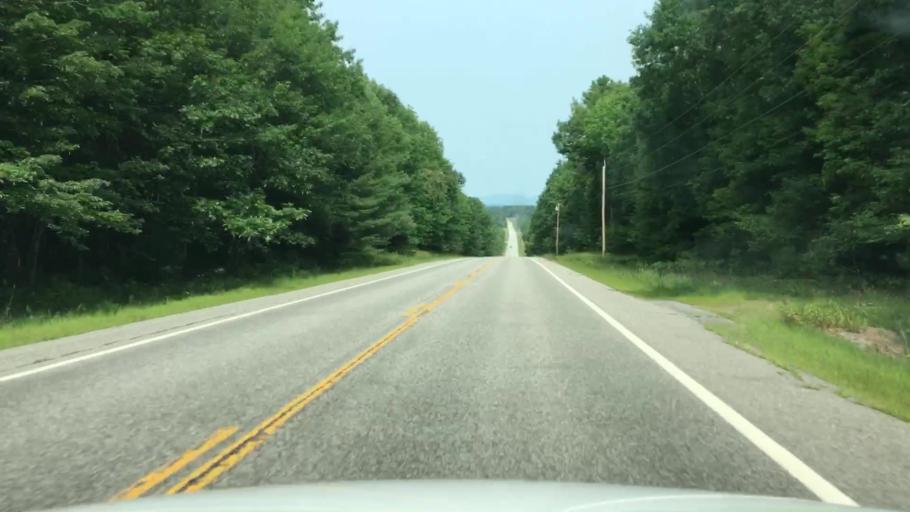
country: US
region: Maine
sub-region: Kennebec County
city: Wayne
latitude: 44.3801
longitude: -70.1024
